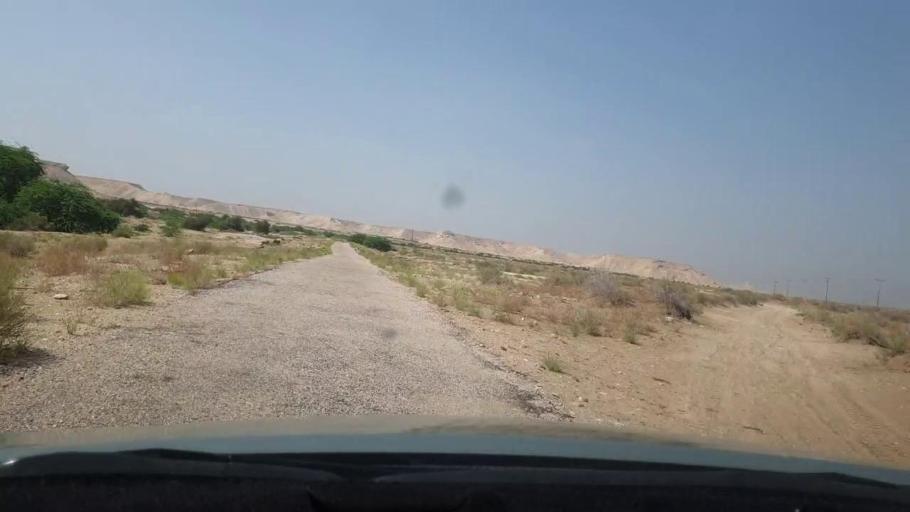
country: PK
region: Sindh
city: Kot Diji
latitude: 27.3318
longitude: 68.8163
